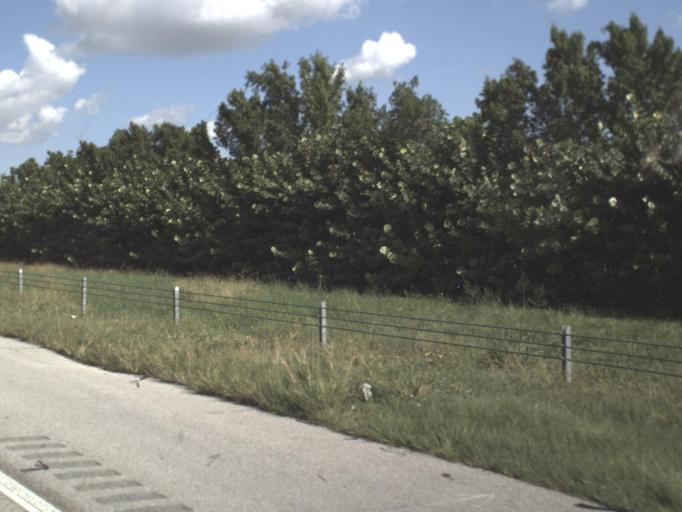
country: US
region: Florida
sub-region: Palm Beach County
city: Boca Del Mar
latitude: 26.3611
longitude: -80.1706
